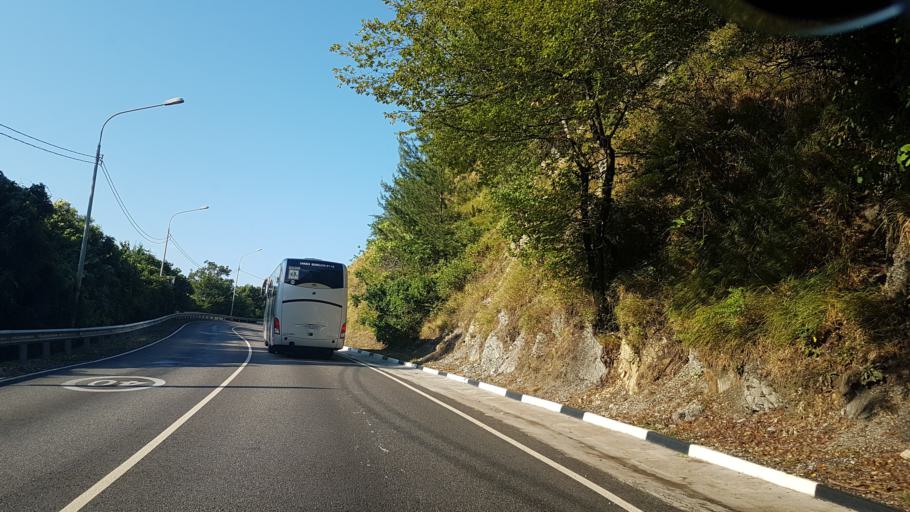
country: RU
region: Krasnodarskiy
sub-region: Sochi City
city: Lazarevskoye
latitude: 43.8542
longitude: 39.4088
